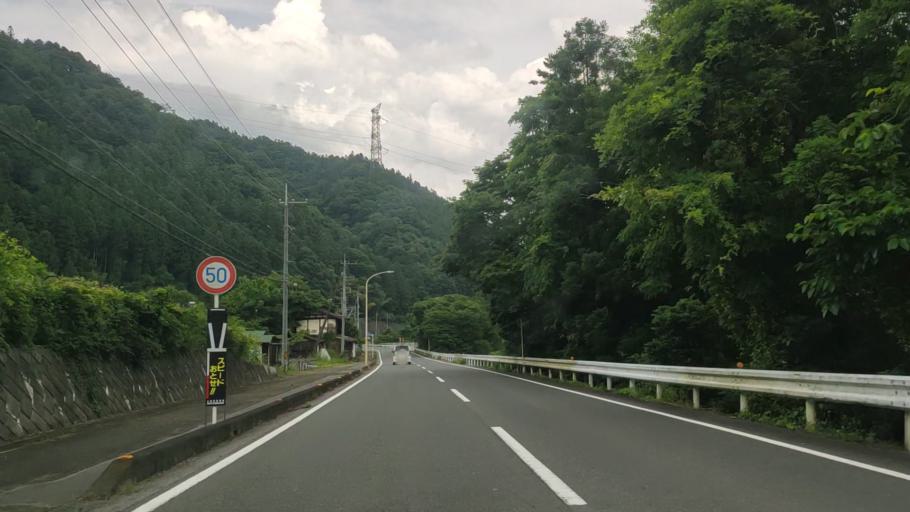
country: JP
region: Saitama
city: Chichibu
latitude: 36.0351
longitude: 138.9227
